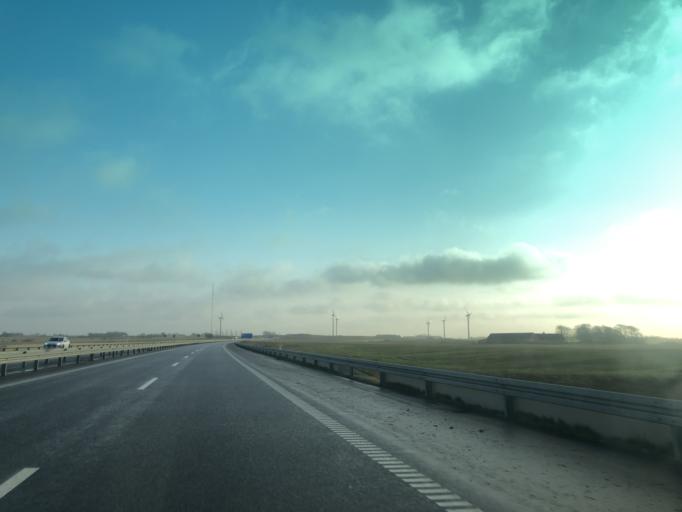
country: DK
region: Central Jutland
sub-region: Holstebro Kommune
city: Holstebro
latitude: 56.3886
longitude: 8.6366
